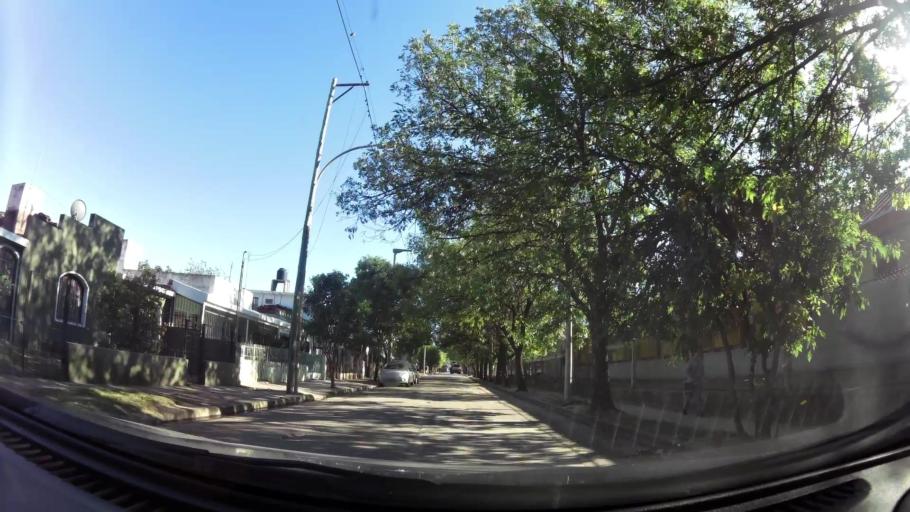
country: AR
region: Cordoba
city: Villa Allende
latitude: -31.3370
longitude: -64.2465
